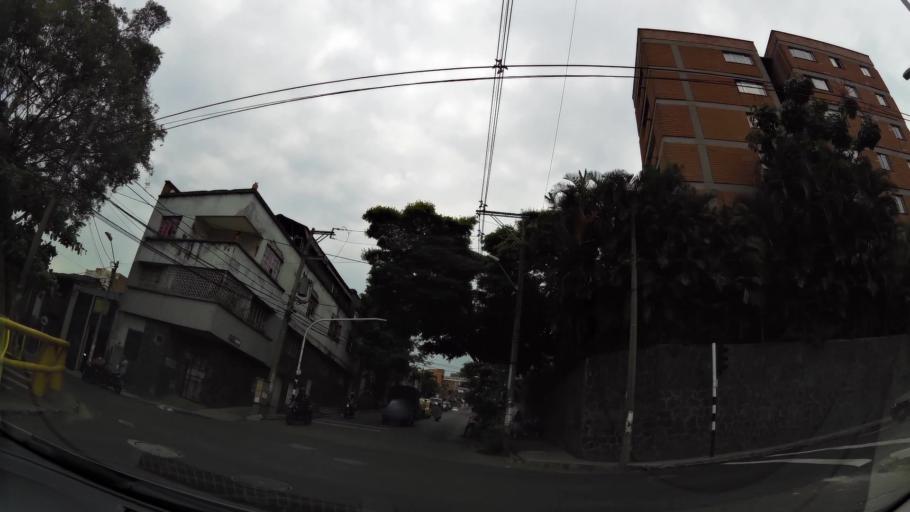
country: CO
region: Antioquia
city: Medellin
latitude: 6.2516
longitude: -75.5585
